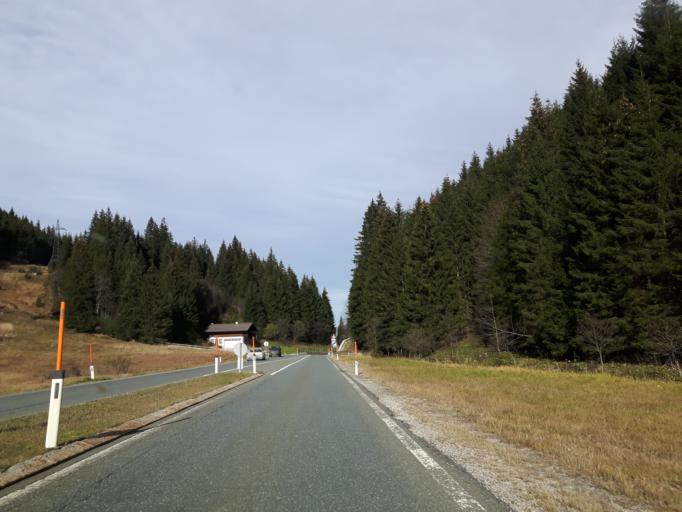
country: AT
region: Tyrol
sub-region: Politischer Bezirk Kitzbuhel
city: Jochberg
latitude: 47.3353
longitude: 12.4068
